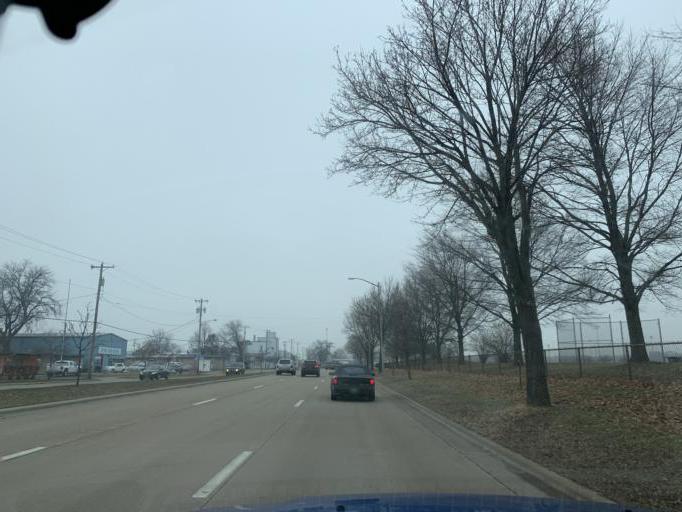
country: US
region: Wisconsin
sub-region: Dane County
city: Maple Bluff
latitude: 43.1010
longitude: -89.3591
